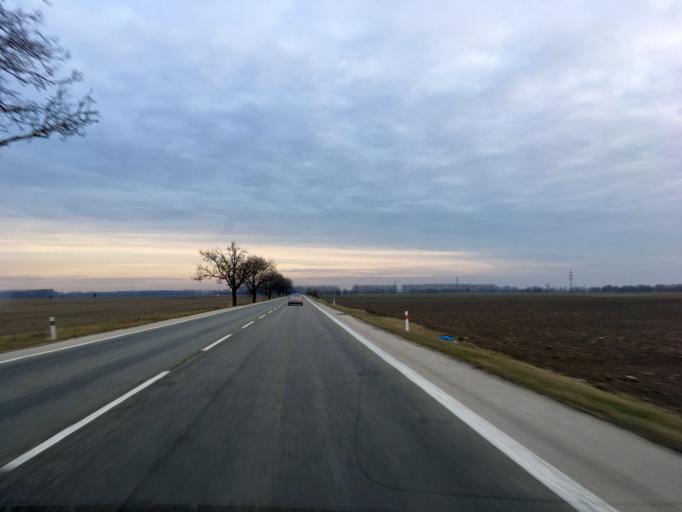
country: SK
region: Trnavsky
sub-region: Okres Dunajska Streda
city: Velky Meder
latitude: 47.9245
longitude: 17.7236
